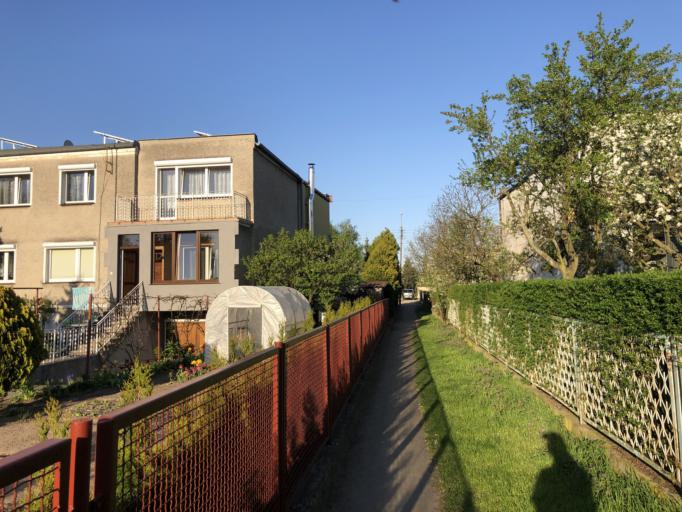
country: PL
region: Greater Poland Voivodeship
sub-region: Powiat poznanski
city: Lubon
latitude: 52.3658
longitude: 16.8816
